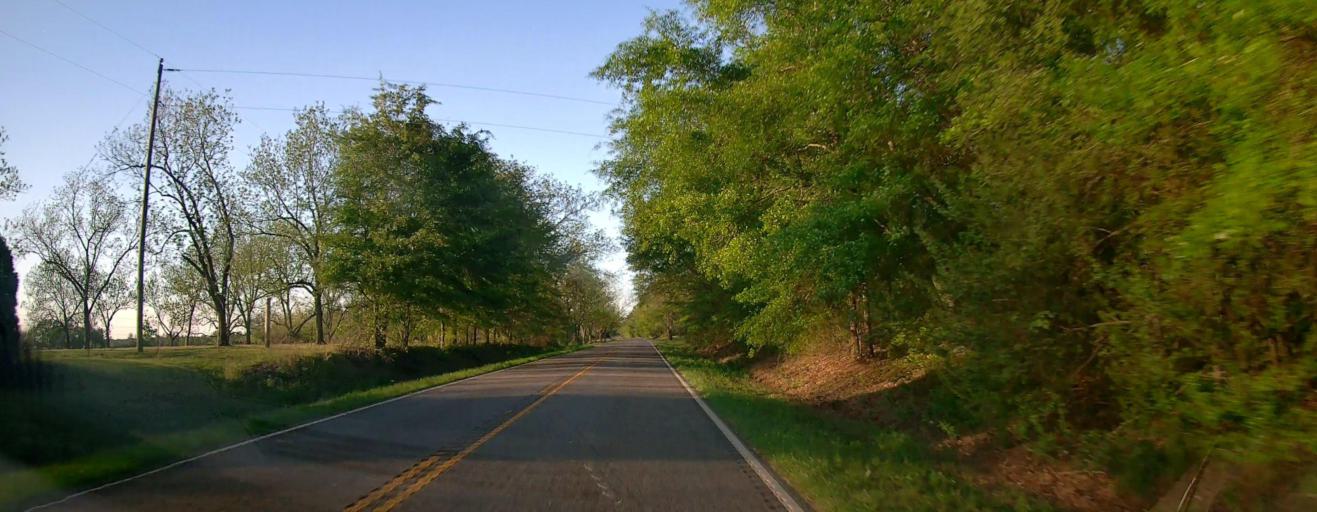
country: US
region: Georgia
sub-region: Marion County
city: Buena Vista
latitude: 32.4076
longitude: -84.4382
